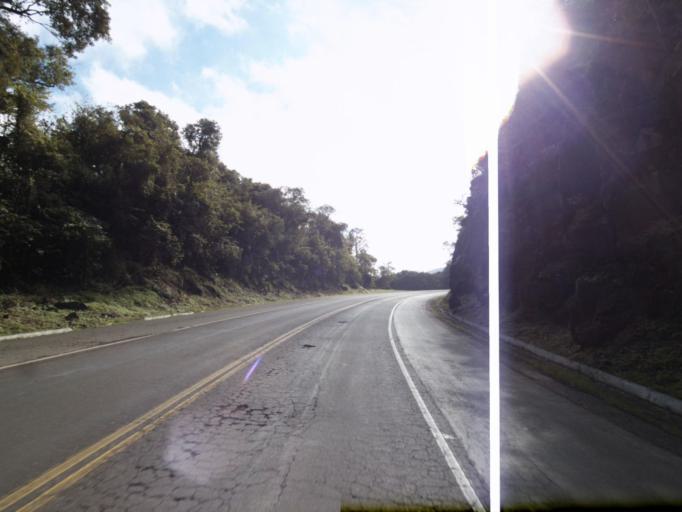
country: BR
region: Rio Grande do Sul
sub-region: Frederico Westphalen
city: Frederico Westphalen
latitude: -27.1540
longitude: -53.2167
